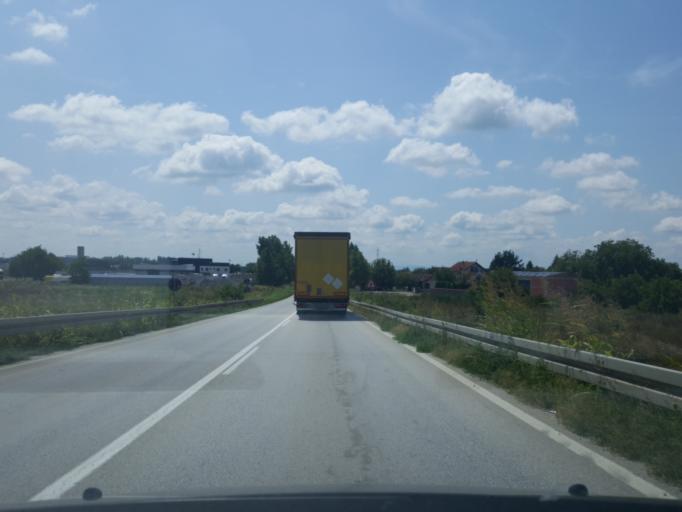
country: RS
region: Autonomna Pokrajina Vojvodina
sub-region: Sremski Okrug
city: Sremska Mitrovica
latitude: 44.9829
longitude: 19.6393
